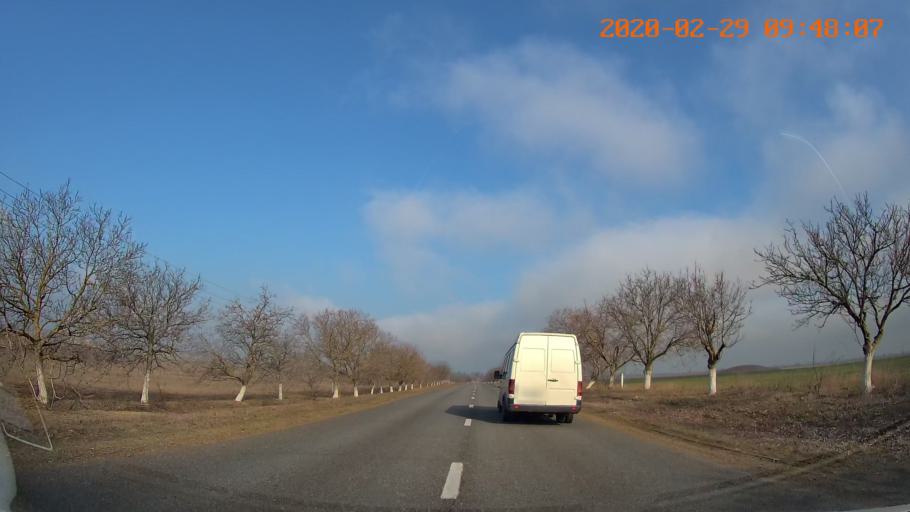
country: MD
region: Telenesti
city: Crasnoe
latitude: 46.6839
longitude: 29.7866
